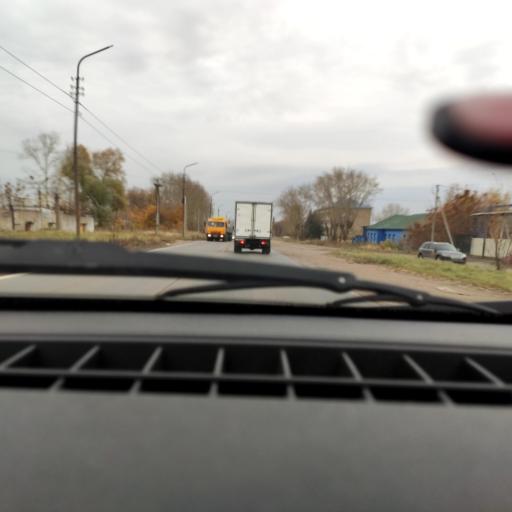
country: RU
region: Bashkortostan
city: Ufa
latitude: 54.8568
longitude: 56.1004
